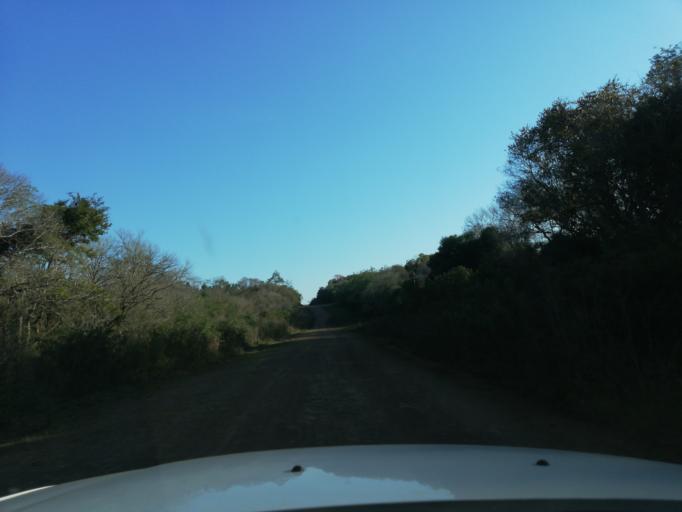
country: AR
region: Misiones
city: Cerro Cora
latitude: -27.5922
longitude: -55.6930
